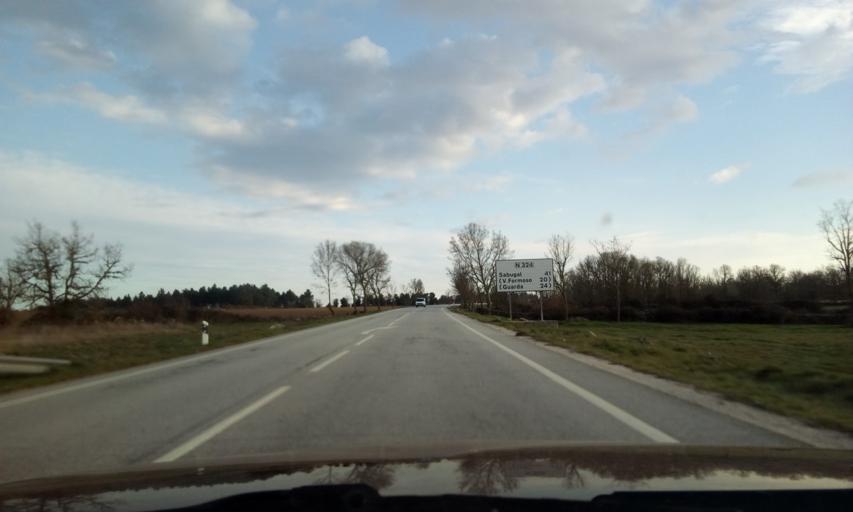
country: PT
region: Guarda
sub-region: Pinhel
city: Pinhel
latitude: 40.6592
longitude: -6.9677
